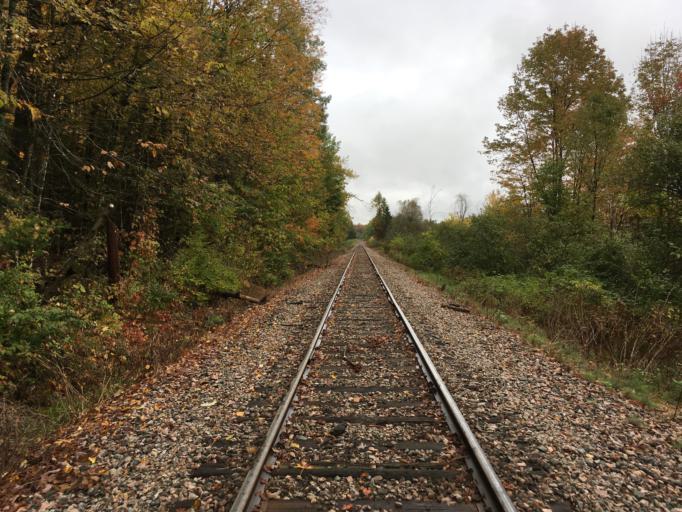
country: US
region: Vermont
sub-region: Orleans County
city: Newport
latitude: 44.8590
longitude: -72.2063
